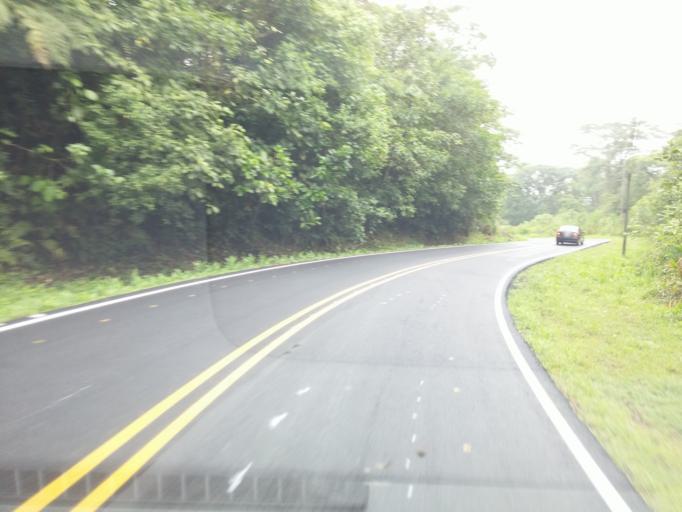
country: CR
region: Alajuela
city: San Ramon
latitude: 10.2032
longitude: -84.5290
